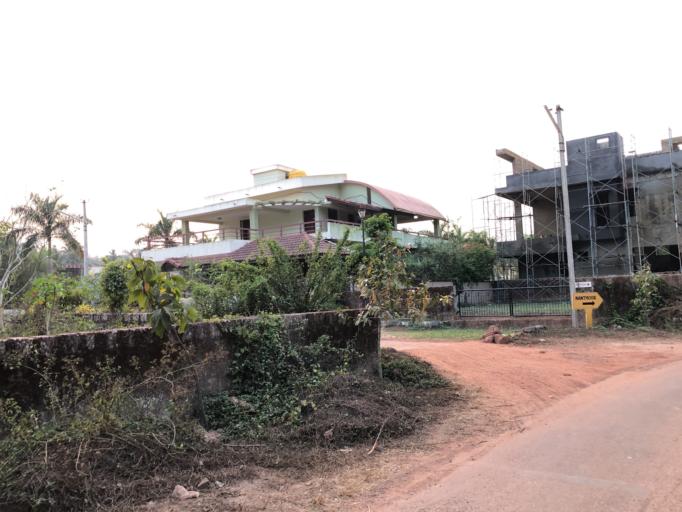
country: IN
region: Karnataka
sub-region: Dakshina Kannada
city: Mangalore
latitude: 12.8903
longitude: 74.8657
